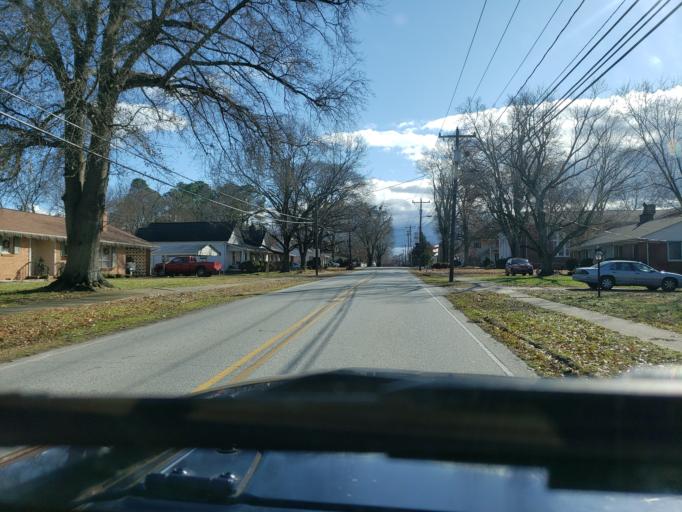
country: US
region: North Carolina
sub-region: Cleveland County
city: White Plains
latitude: 35.1736
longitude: -81.4496
